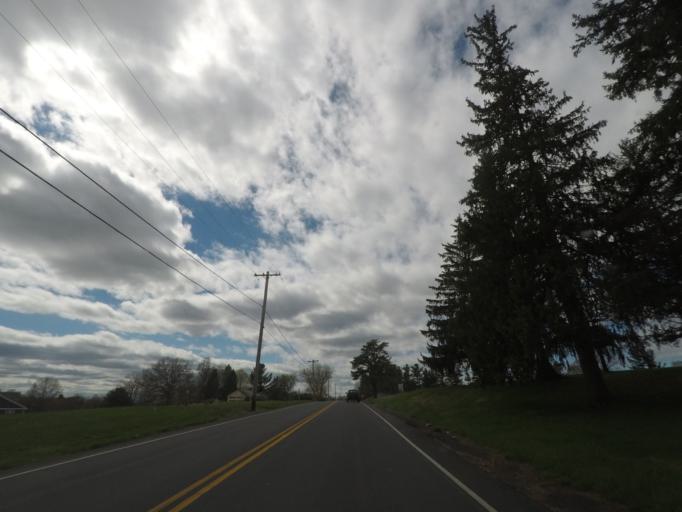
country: US
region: New York
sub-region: Columbia County
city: Valatie
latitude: 42.4006
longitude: -73.6665
